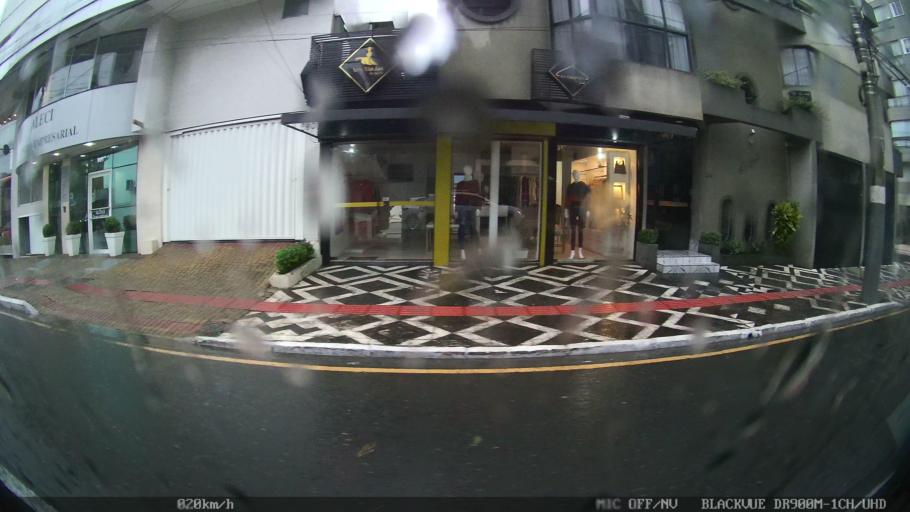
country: BR
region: Santa Catarina
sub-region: Balneario Camboriu
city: Balneario Camboriu
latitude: -26.9914
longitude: -48.6374
